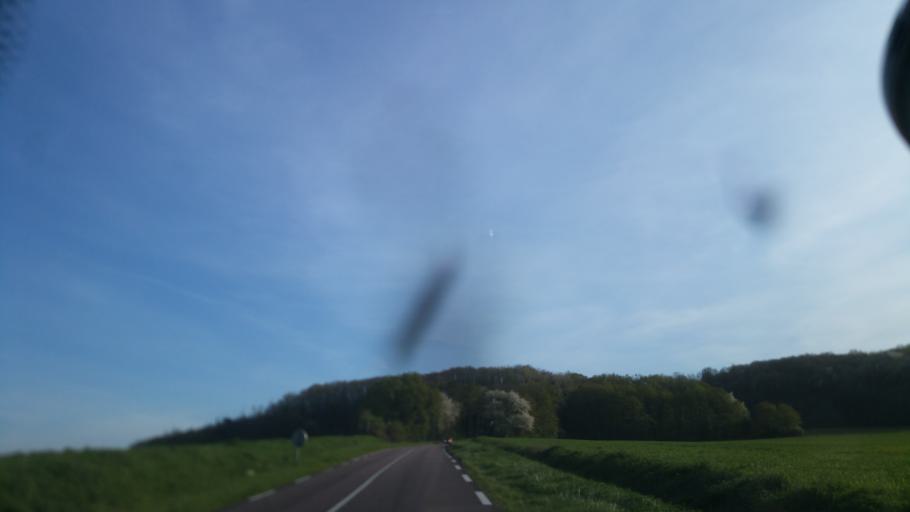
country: FR
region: Ile-de-France
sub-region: Departement de l'Essonne
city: Saint-Cyr-sous-Dourdan
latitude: 48.5549
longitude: 2.0263
